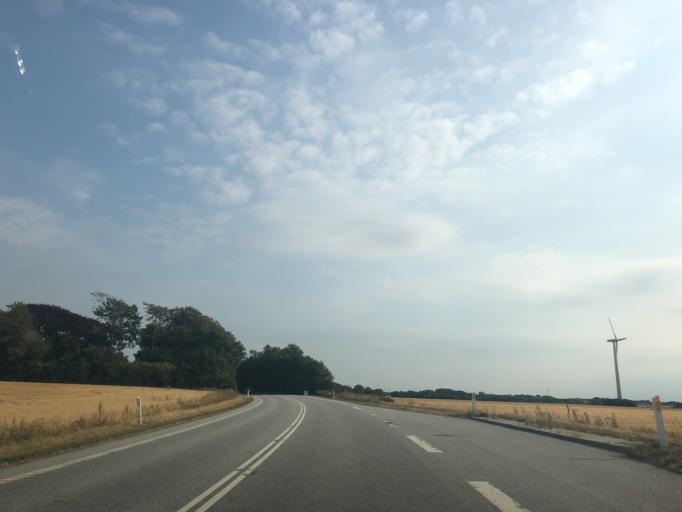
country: DK
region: Central Jutland
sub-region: Skive Kommune
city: Skive
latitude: 56.6402
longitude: 8.9196
